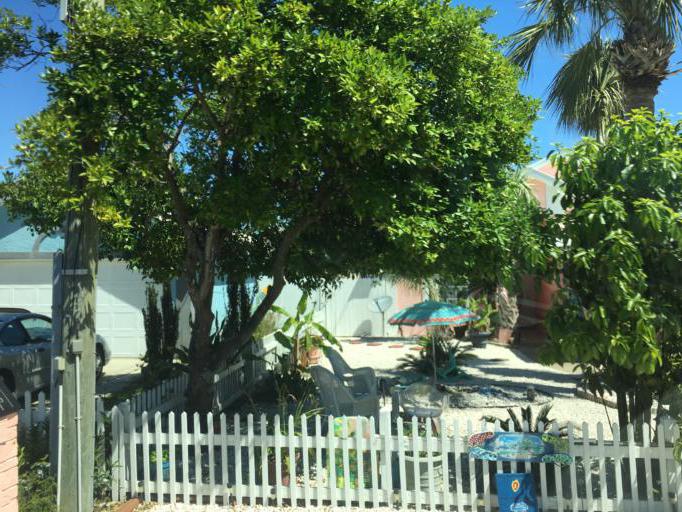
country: US
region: Florida
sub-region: Bay County
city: Panama City Beach
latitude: 30.2055
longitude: -85.8497
